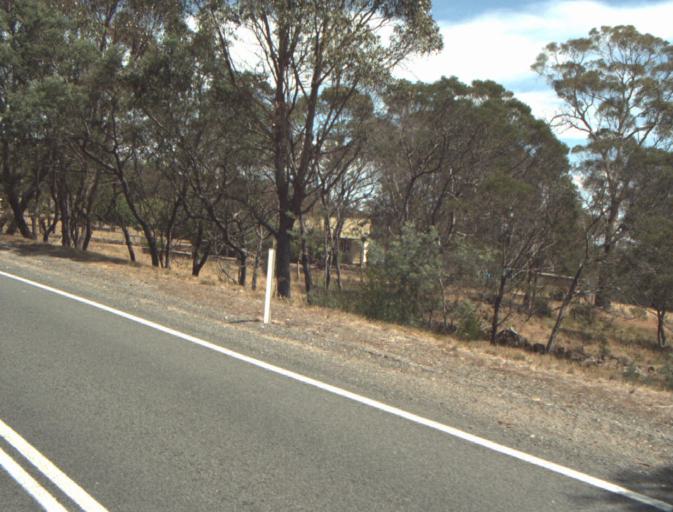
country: AU
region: Tasmania
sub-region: Launceston
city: Mayfield
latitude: -41.3437
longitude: 147.1409
